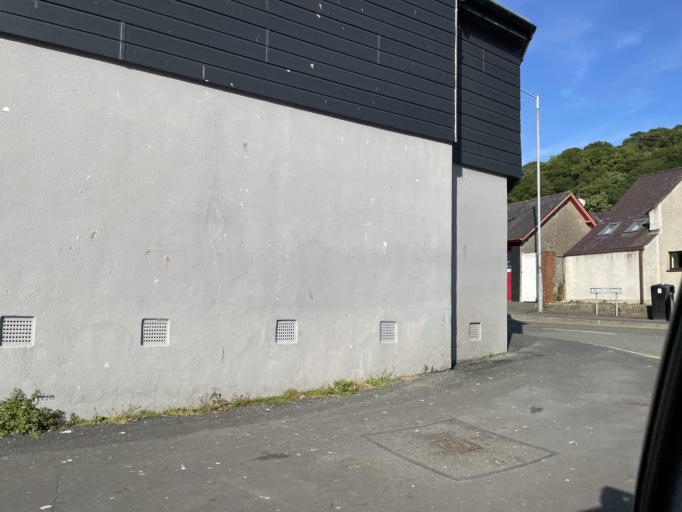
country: GB
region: Wales
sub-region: Gwynedd
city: Bangor
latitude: 53.2289
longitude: -4.1235
